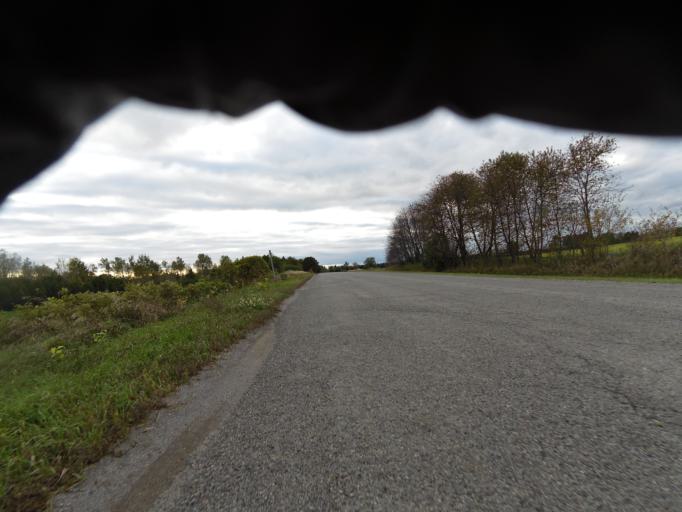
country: CA
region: Ontario
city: Cobourg
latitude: 43.9786
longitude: -77.9327
